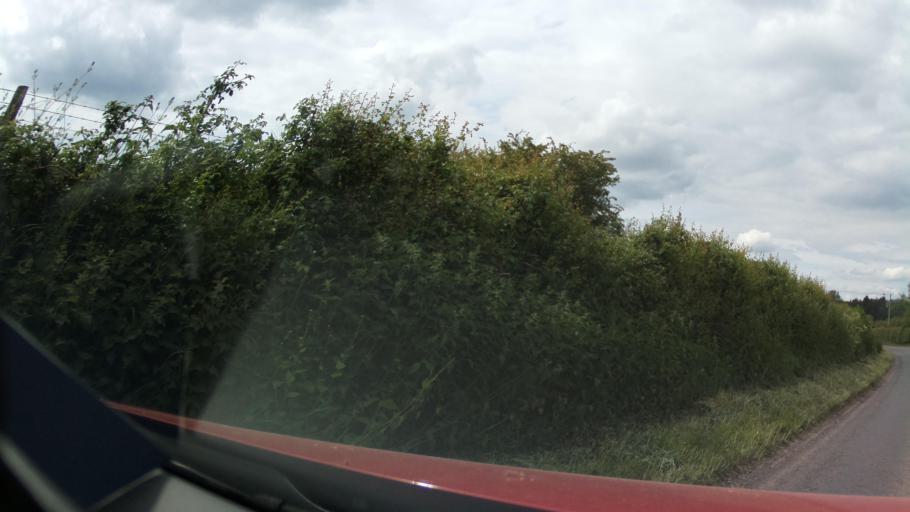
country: GB
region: England
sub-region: Herefordshire
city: Ledbury
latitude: 52.0625
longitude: -2.4449
